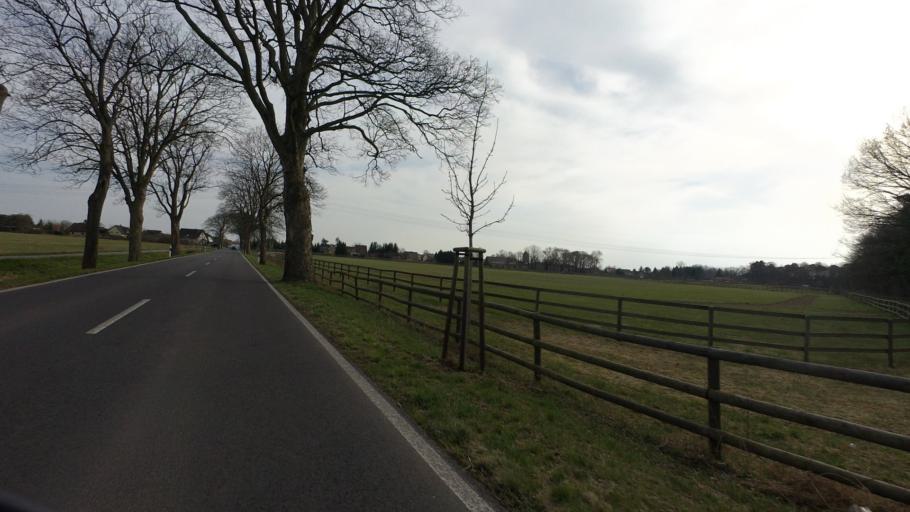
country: DE
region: Brandenburg
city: Stahnsdorf
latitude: 52.3444
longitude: 13.1983
